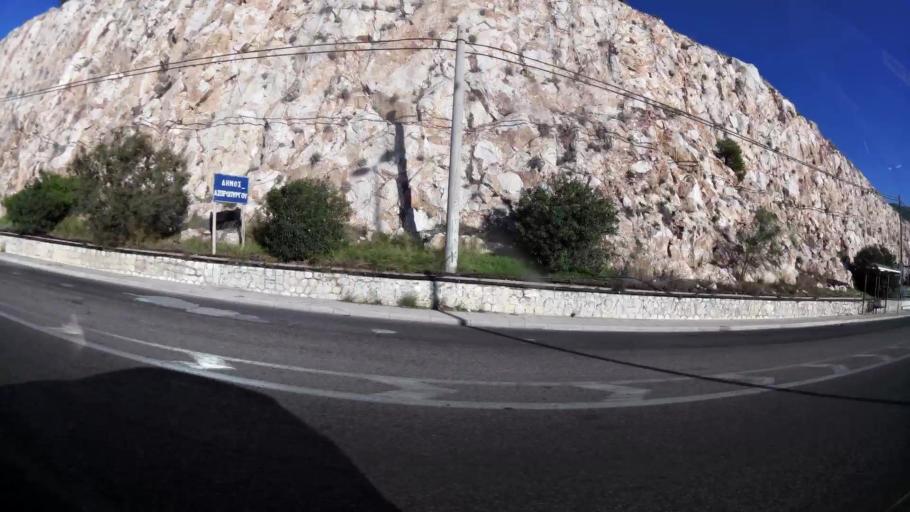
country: GR
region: Attica
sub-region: Nomarchia Athinas
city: Skaramangas
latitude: 38.0160
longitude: 23.5986
